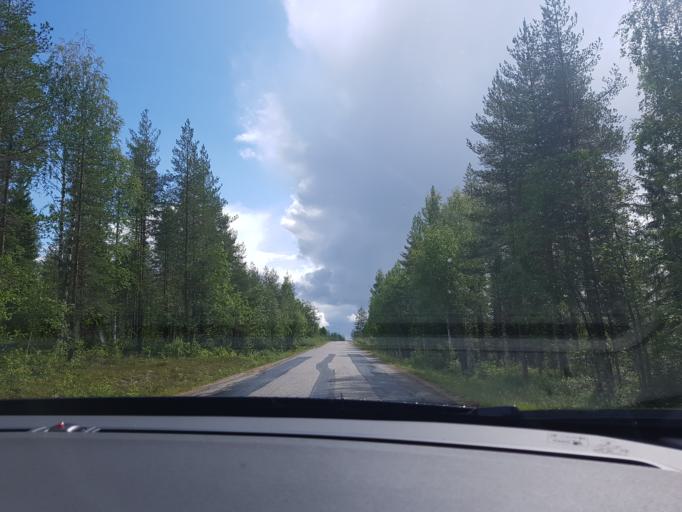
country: FI
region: Kainuu
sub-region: Kehys-Kainuu
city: Kuhmo
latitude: 64.4585
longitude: 29.6417
